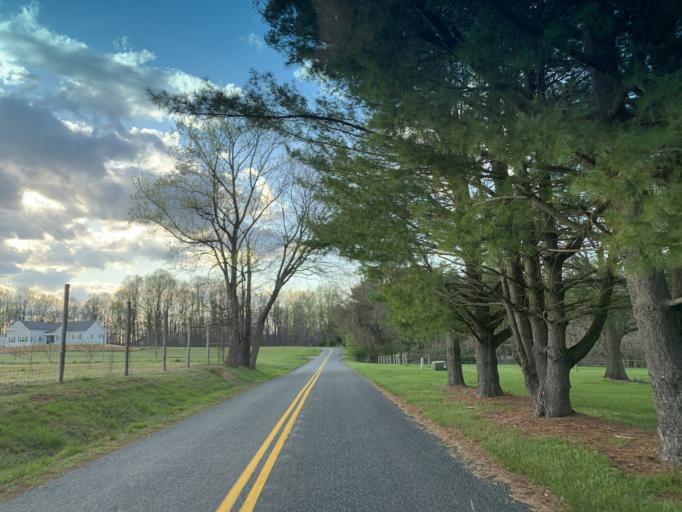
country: US
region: Maryland
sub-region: Harford County
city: South Bel Air
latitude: 39.6125
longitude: -76.2989
